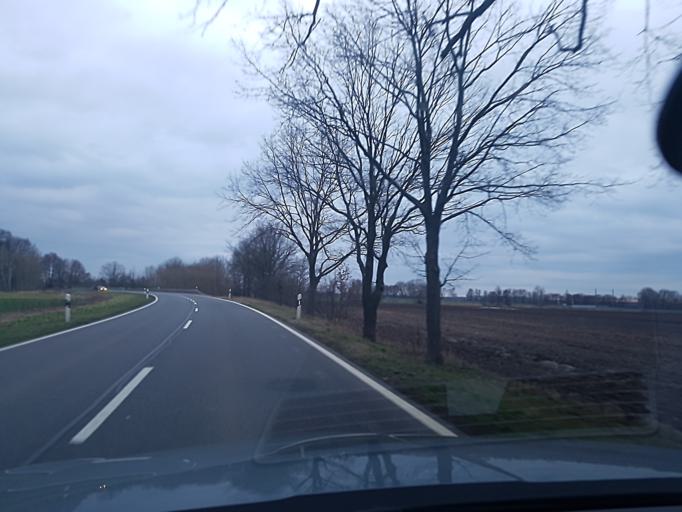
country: DE
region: Brandenburg
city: Schonewalde
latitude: 51.6676
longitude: 13.5885
